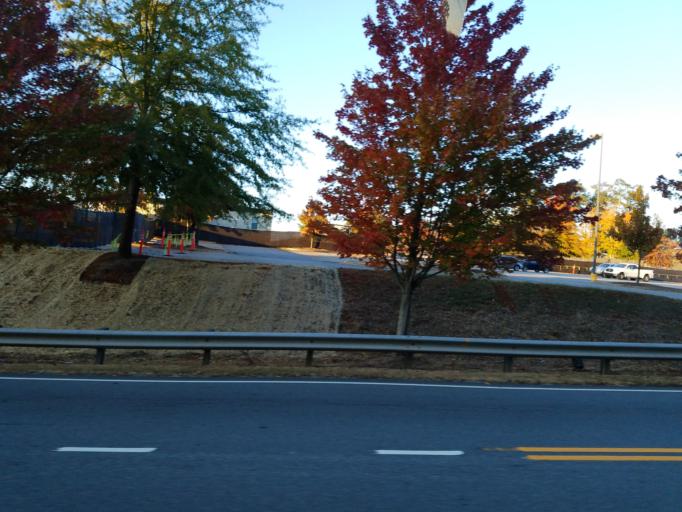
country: US
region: Georgia
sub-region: Lumpkin County
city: Dahlonega
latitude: 34.5247
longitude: -83.9861
